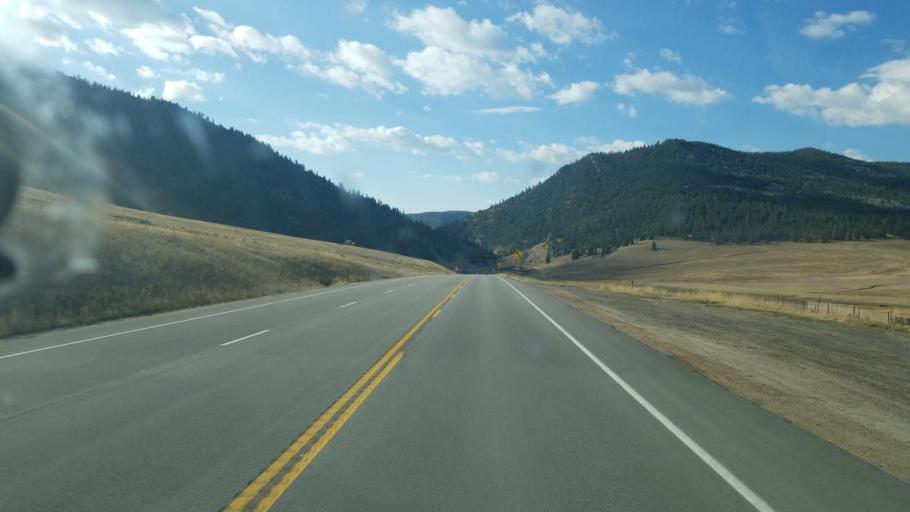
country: US
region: Colorado
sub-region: Chaffee County
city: Buena Vista
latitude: 38.8700
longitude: -105.9845
